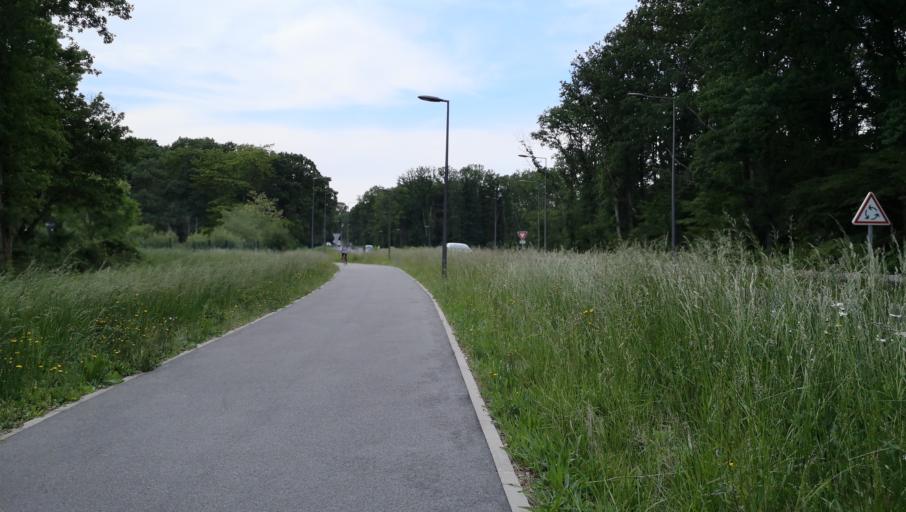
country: FR
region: Centre
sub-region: Departement du Loiret
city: Saran
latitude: 47.9574
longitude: 1.9010
